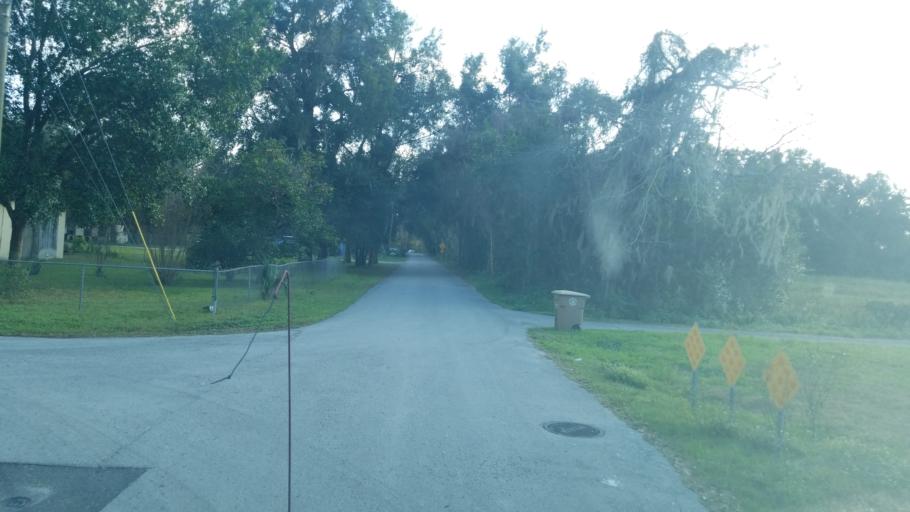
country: US
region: Florida
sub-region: Marion County
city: Ocala
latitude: 29.1819
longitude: -82.1645
